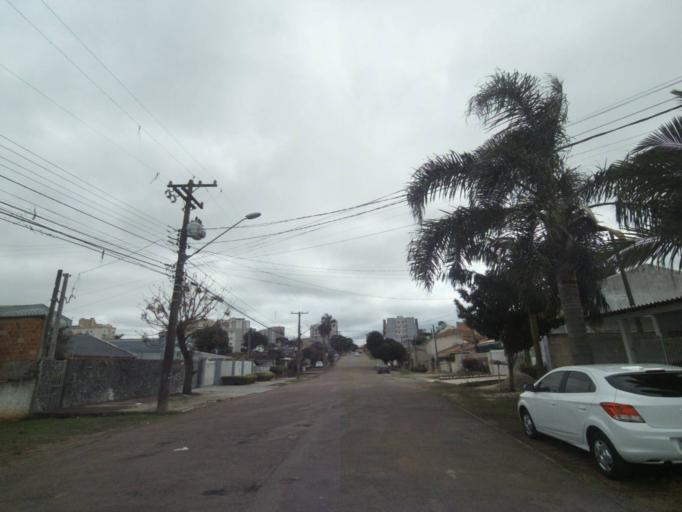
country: BR
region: Parana
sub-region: Curitiba
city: Curitiba
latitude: -25.5018
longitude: -49.2896
